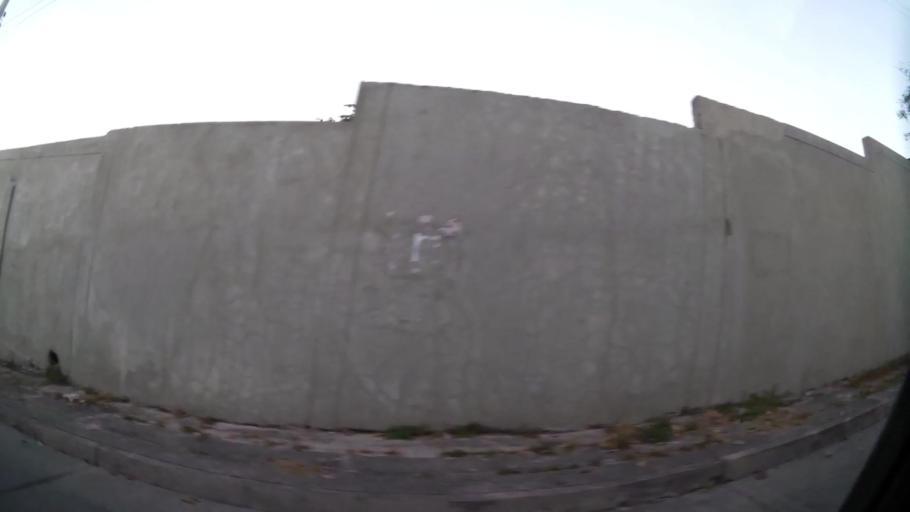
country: CO
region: Bolivar
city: Cartagena
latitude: 10.4003
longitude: -75.5140
